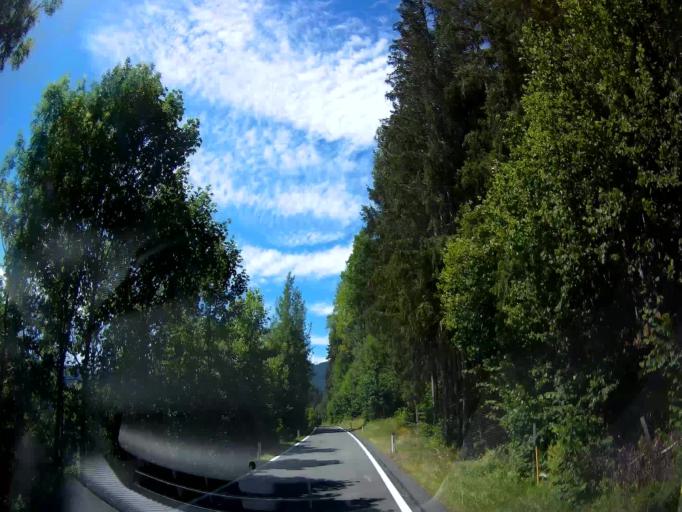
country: AT
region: Carinthia
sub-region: Politischer Bezirk Sankt Veit an der Glan
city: Glodnitz
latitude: 46.9072
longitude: 14.0970
